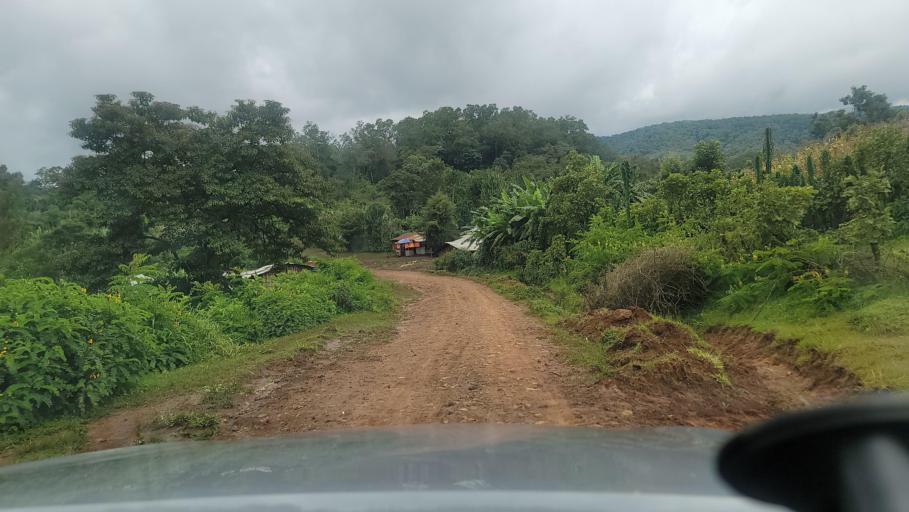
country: ET
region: Southern Nations, Nationalities, and People's Region
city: Bonga
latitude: 7.6338
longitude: 36.2224
